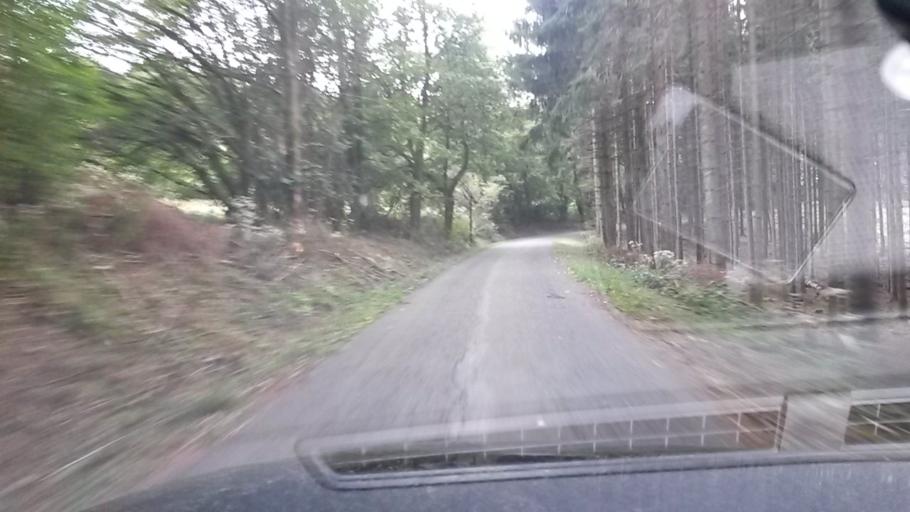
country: DE
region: North Rhine-Westphalia
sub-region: Regierungsbezirk Arnsberg
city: Herscheid
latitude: 51.2063
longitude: 7.7575
